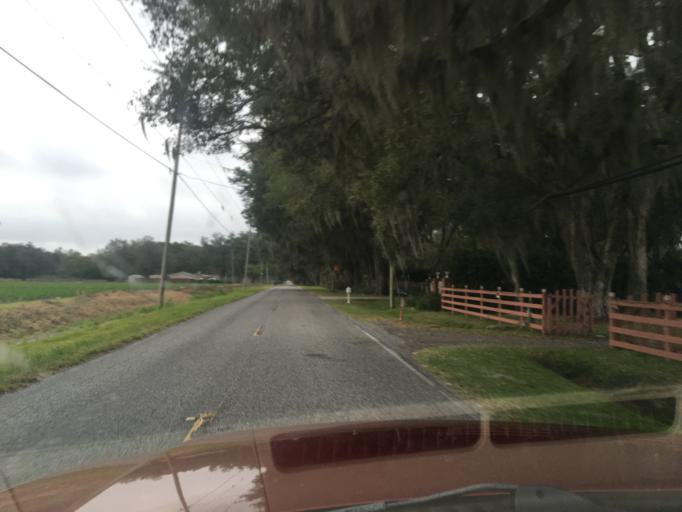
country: US
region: Florida
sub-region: Hillsborough County
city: Plant City
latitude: 28.0462
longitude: -82.0970
